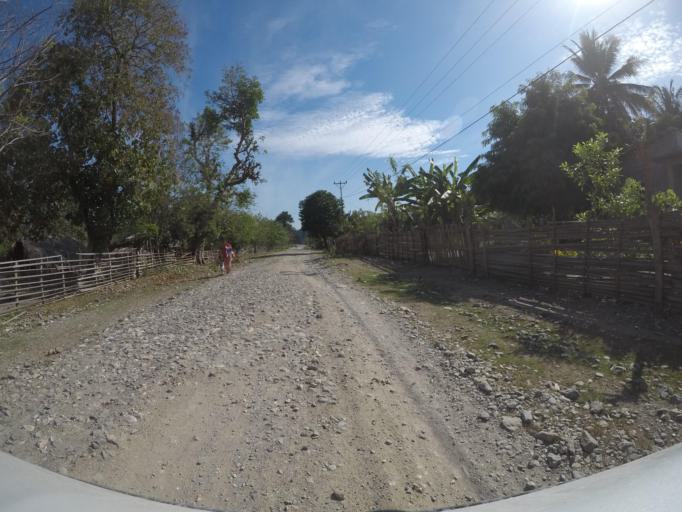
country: TL
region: Bobonaro
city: Maliana
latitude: -8.8552
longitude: 125.2181
